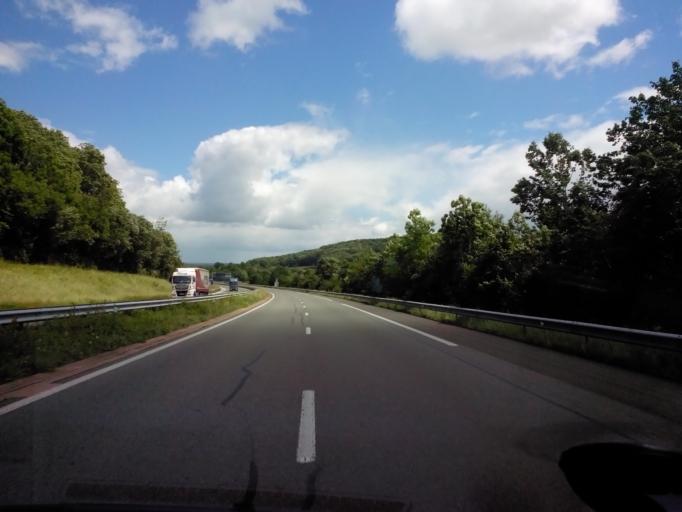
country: FR
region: Champagne-Ardenne
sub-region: Departement de la Haute-Marne
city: Avrecourt
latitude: 47.9669
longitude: 5.4862
